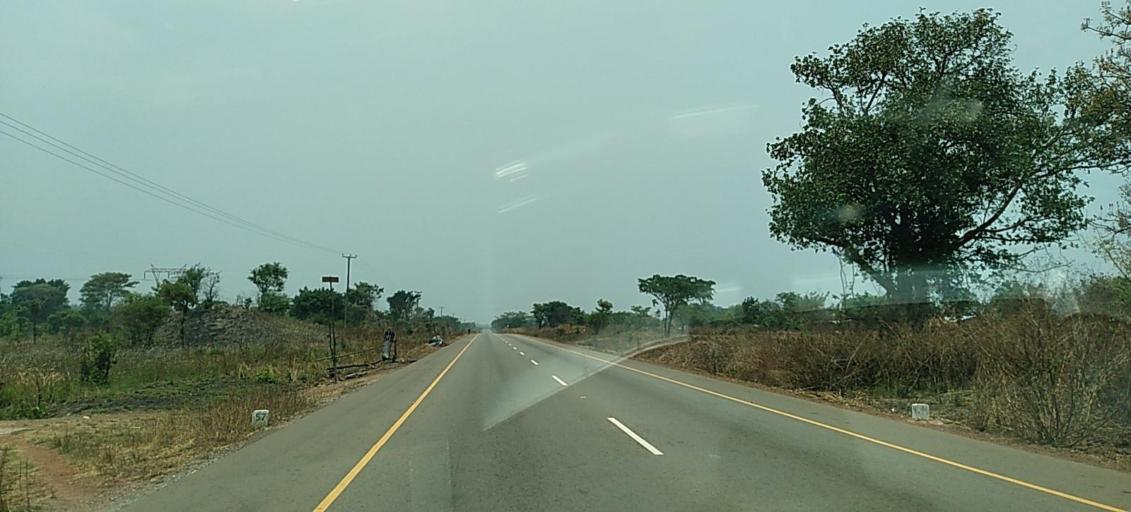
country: ZM
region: Copperbelt
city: Chililabombwe
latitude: -12.3990
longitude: 27.3724
